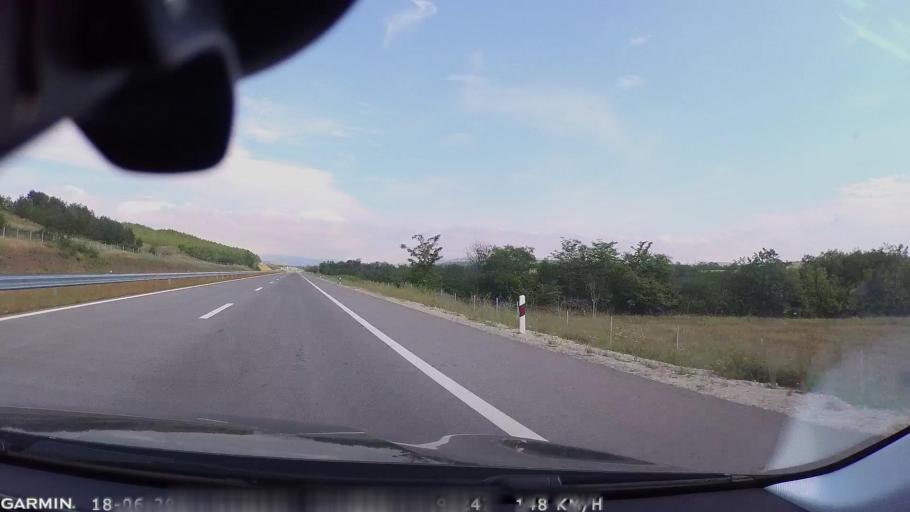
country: MK
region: Sveti Nikole
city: Sveti Nikole
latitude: 41.8969
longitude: 21.9210
